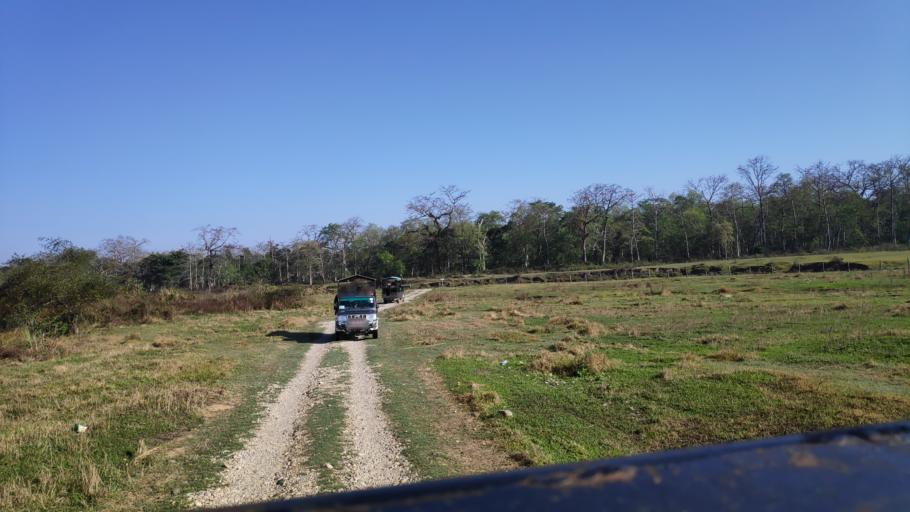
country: NP
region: Central Region
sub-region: Narayani Zone
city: Bharatpur
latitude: 27.5609
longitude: 84.5222
